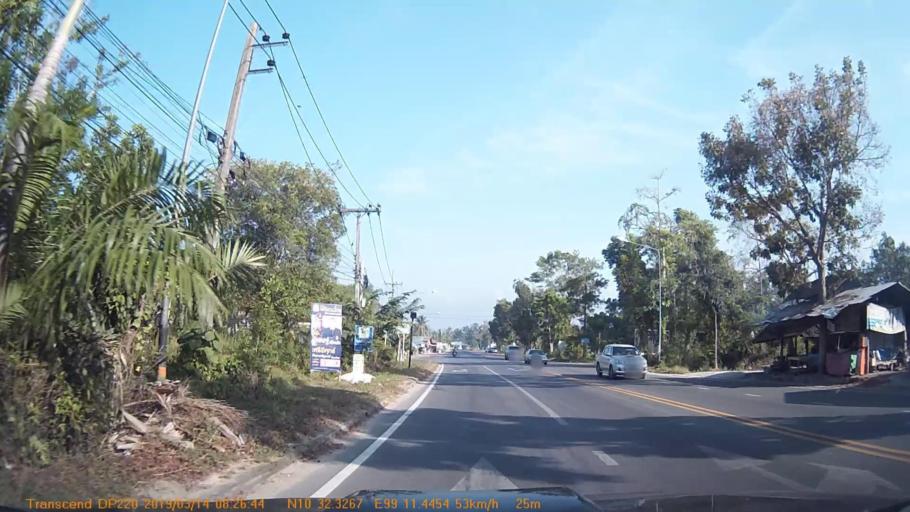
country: TH
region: Chumphon
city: Chumphon
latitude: 10.5389
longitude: 99.1907
